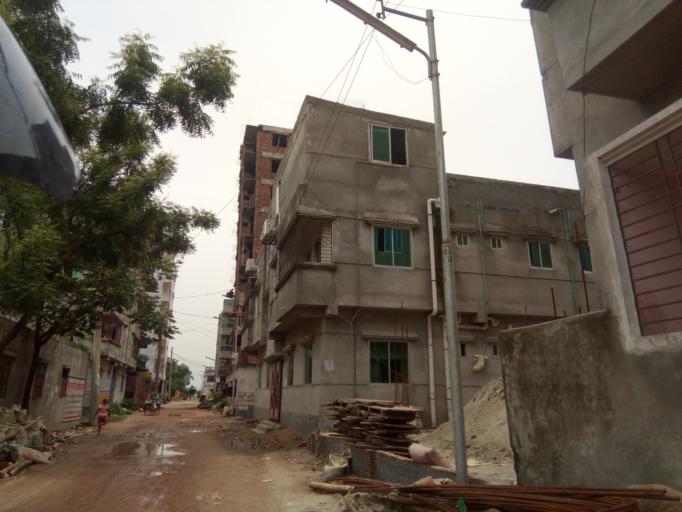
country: BD
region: Dhaka
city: Azimpur
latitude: 23.7426
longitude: 90.3497
